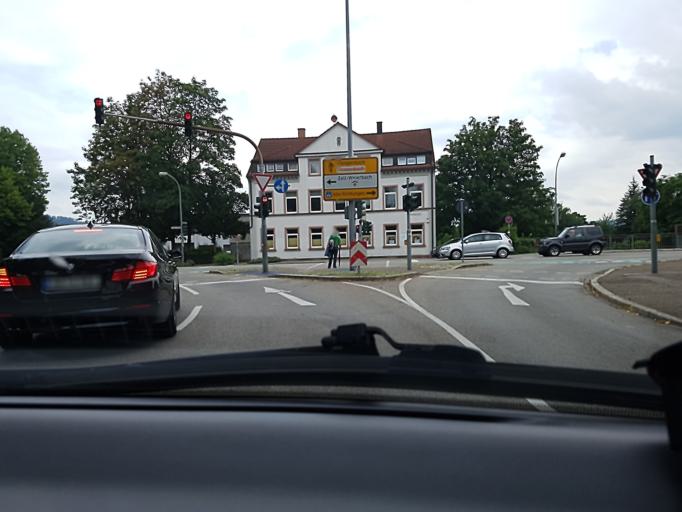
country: DE
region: Baden-Wuerttemberg
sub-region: Freiburg Region
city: Offenburg
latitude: 48.4682
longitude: 7.9490
